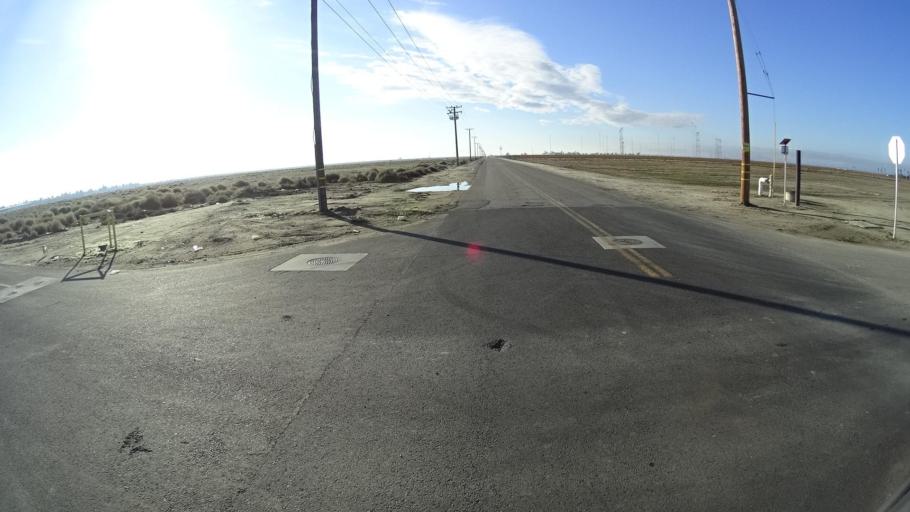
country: US
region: California
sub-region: Kern County
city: Delano
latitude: 35.7687
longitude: -119.2762
